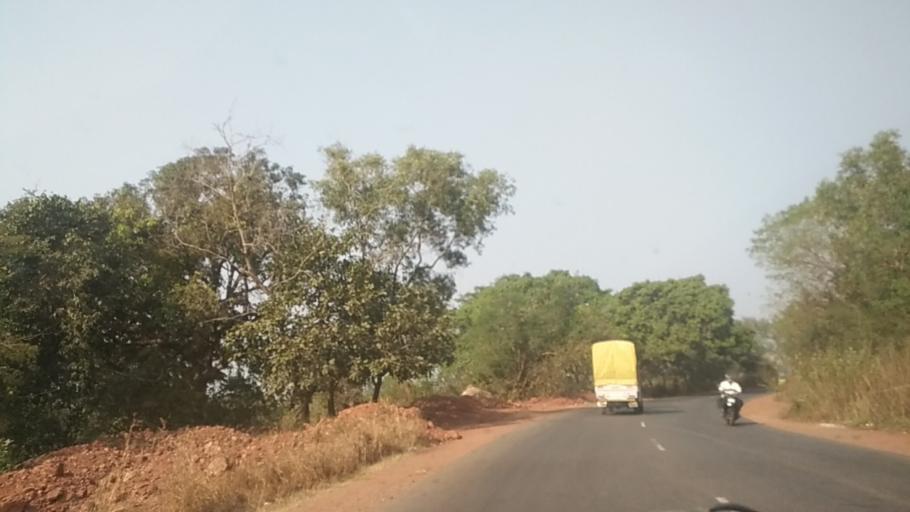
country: IN
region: Goa
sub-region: North Goa
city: Colovale
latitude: 15.6244
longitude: 73.8233
